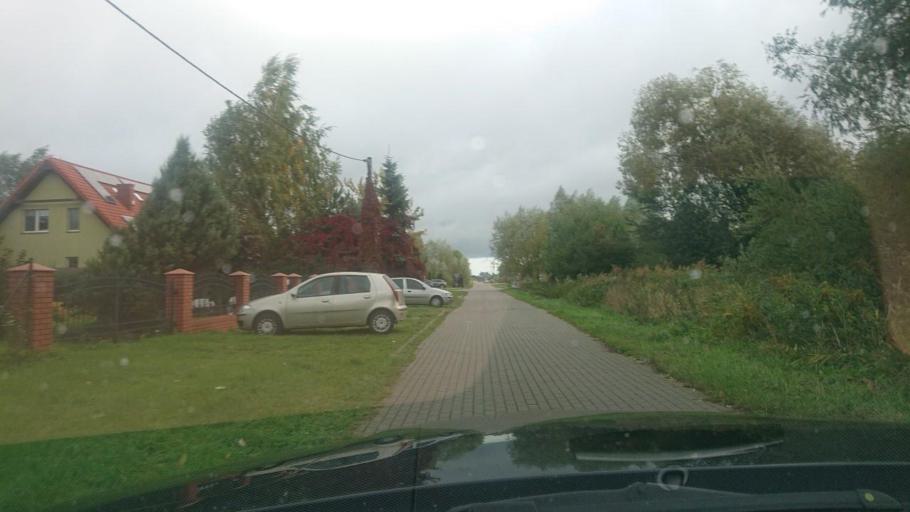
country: PL
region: Greater Poland Voivodeship
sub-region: Powiat gnieznienski
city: Gniezno
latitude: 52.5213
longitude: 17.6343
